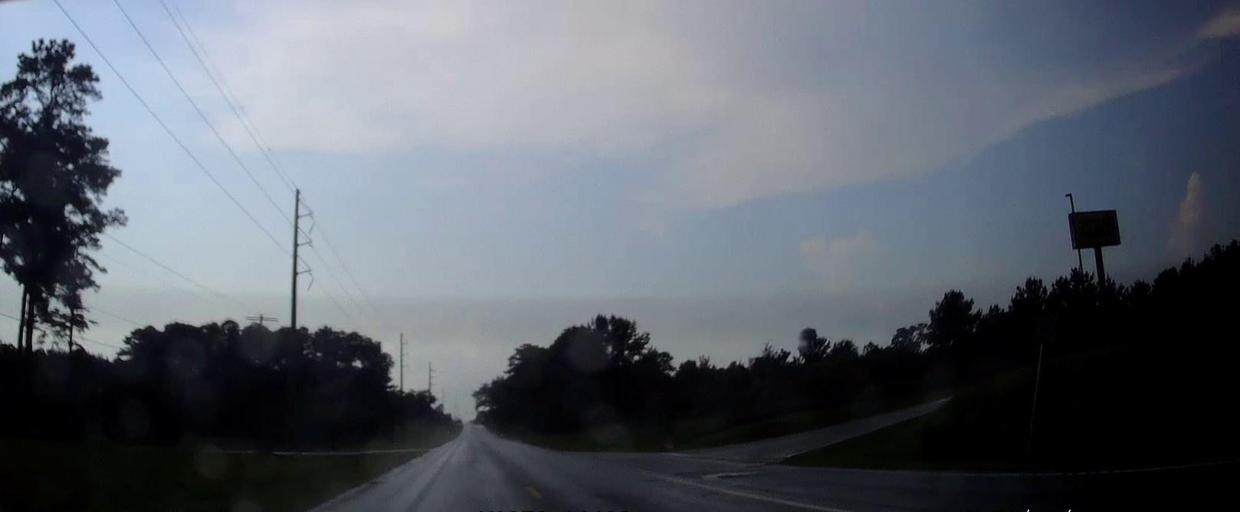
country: US
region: Georgia
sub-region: Twiggs County
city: Jeffersonville
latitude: 32.5879
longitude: -83.2245
